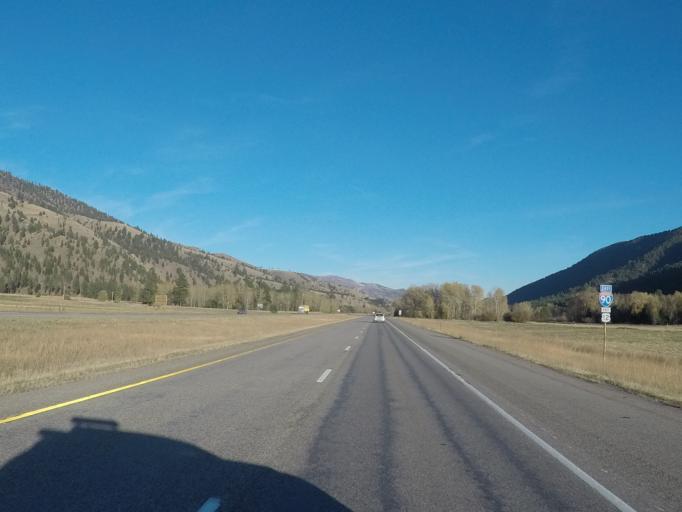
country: US
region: Montana
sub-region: Missoula County
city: Clinton
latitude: 46.7271
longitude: -113.6623
